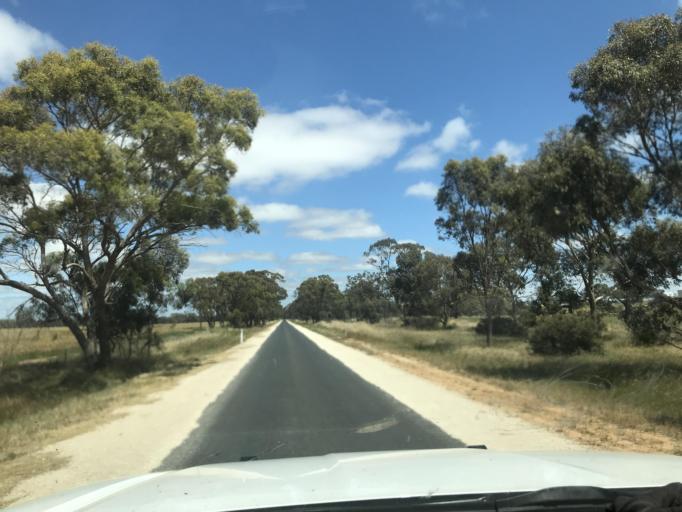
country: AU
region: South Australia
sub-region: Tatiara
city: Bordertown
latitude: -36.3086
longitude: 141.0500
